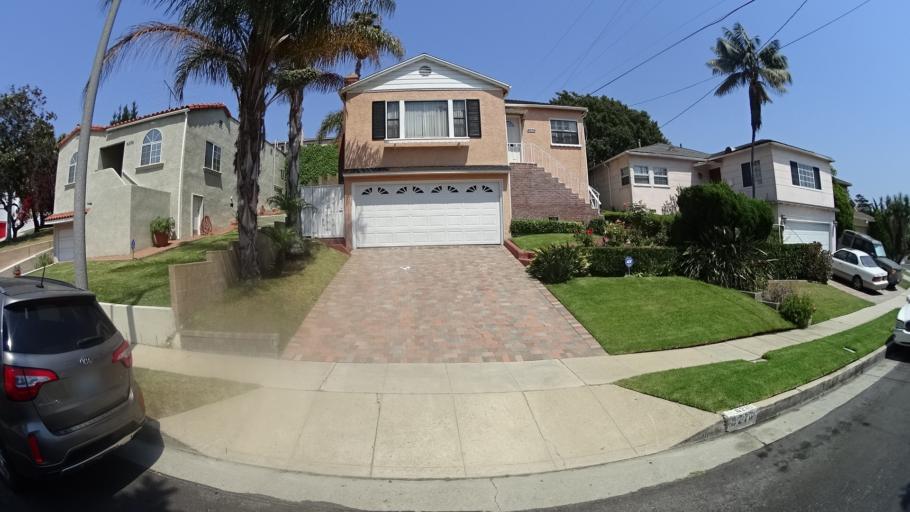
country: US
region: California
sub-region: Los Angeles County
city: View Park-Windsor Hills
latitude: 33.9831
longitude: -118.3512
